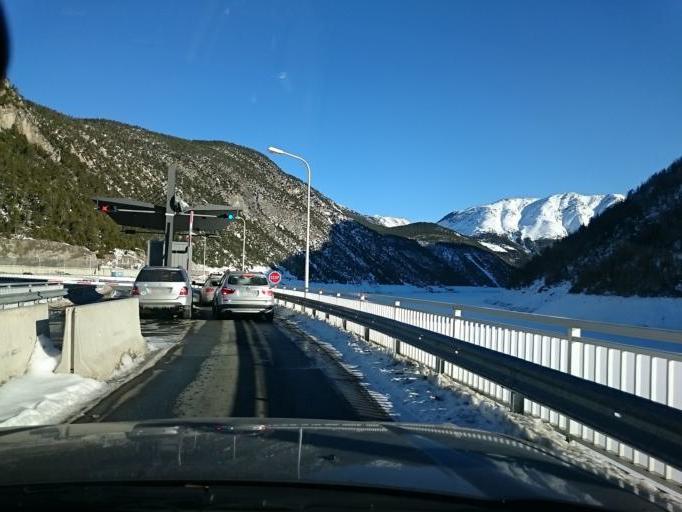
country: IT
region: Lombardy
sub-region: Provincia di Sondrio
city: Livigno
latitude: 46.6233
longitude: 10.1935
